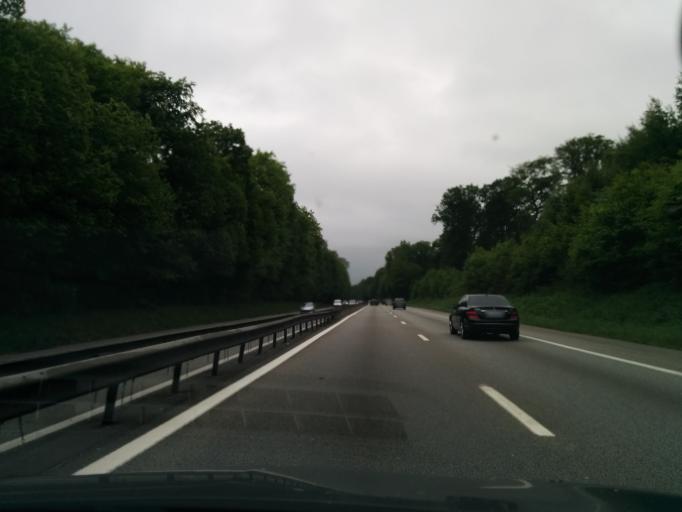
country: FR
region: Ile-de-France
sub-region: Departement des Yvelines
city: Saint-Nom-la-Breteche
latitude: 48.8890
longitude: 2.0106
